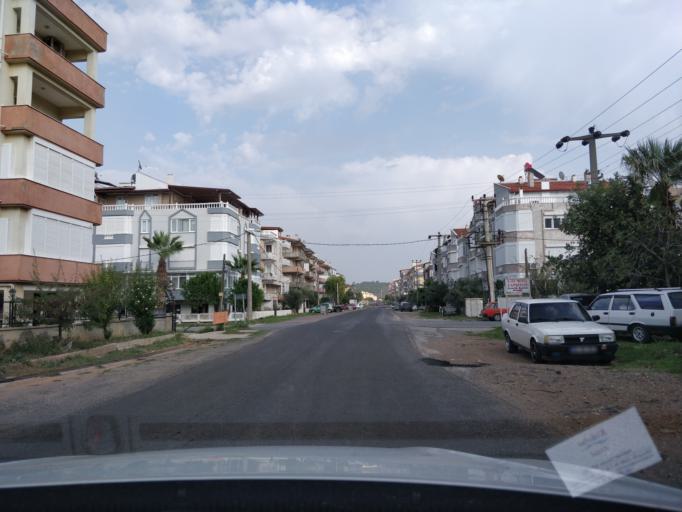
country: TR
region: Balikesir
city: Ayvalik
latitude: 39.2733
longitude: 26.6531
